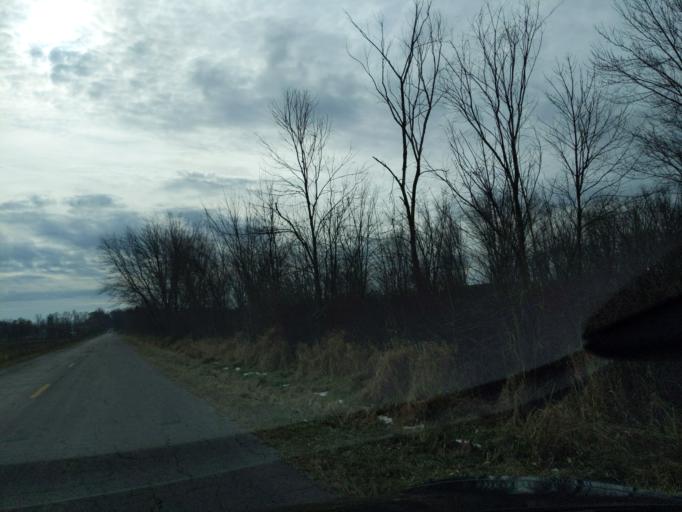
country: US
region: Michigan
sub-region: Ingham County
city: Leslie
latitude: 42.4651
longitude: -84.5020
